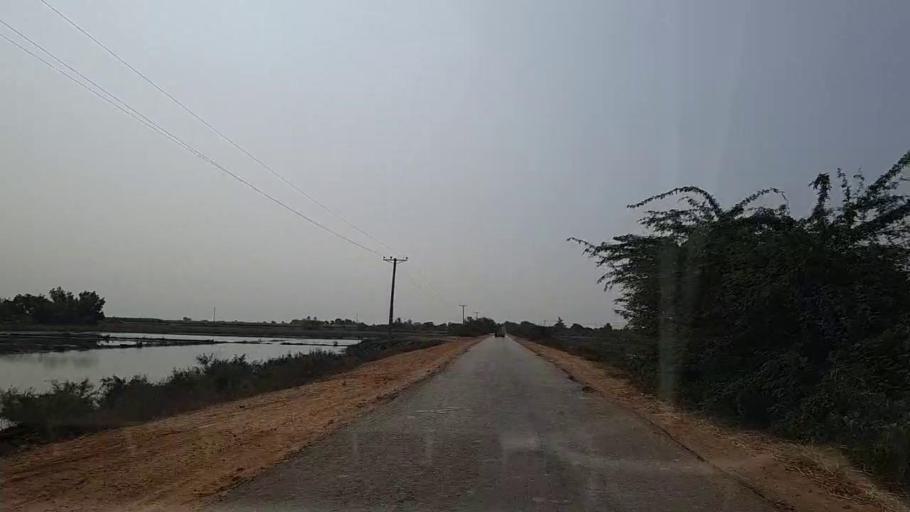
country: PK
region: Sindh
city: Chuhar Jamali
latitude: 24.3761
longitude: 67.9692
